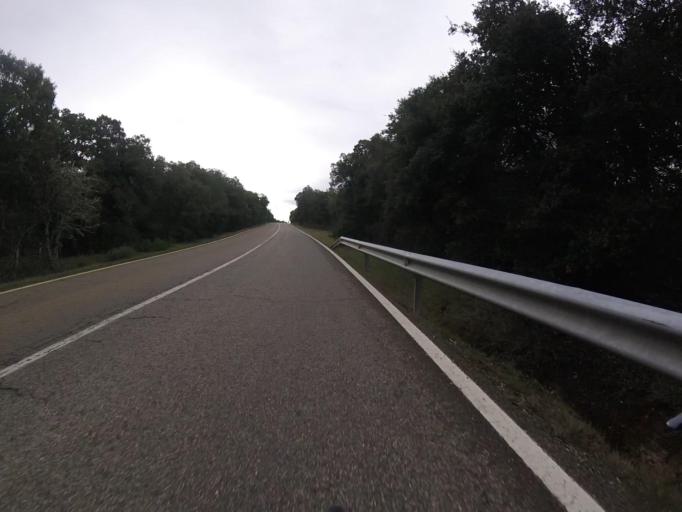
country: ES
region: Navarre
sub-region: Provincia de Navarra
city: Lezaun
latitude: 42.7589
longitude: -2.0127
